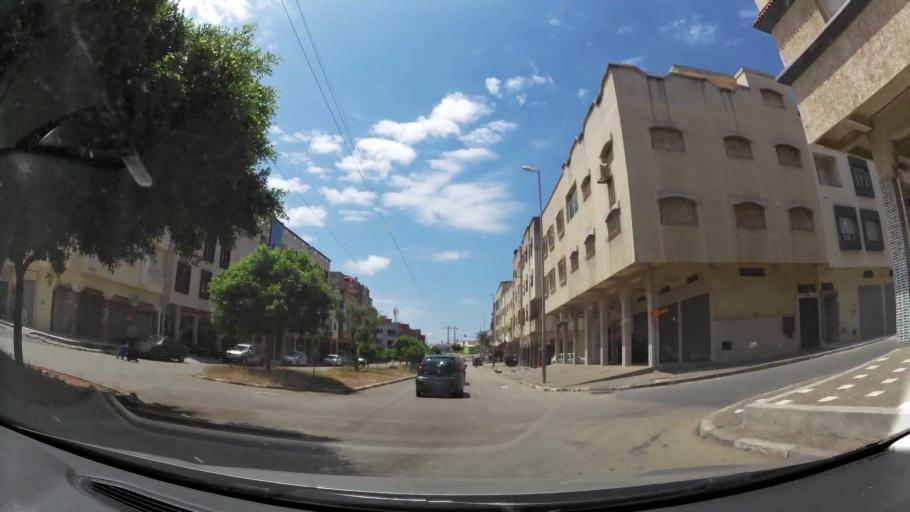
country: MA
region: Gharb-Chrarda-Beni Hssen
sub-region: Kenitra Province
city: Kenitra
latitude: 34.2671
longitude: -6.6160
